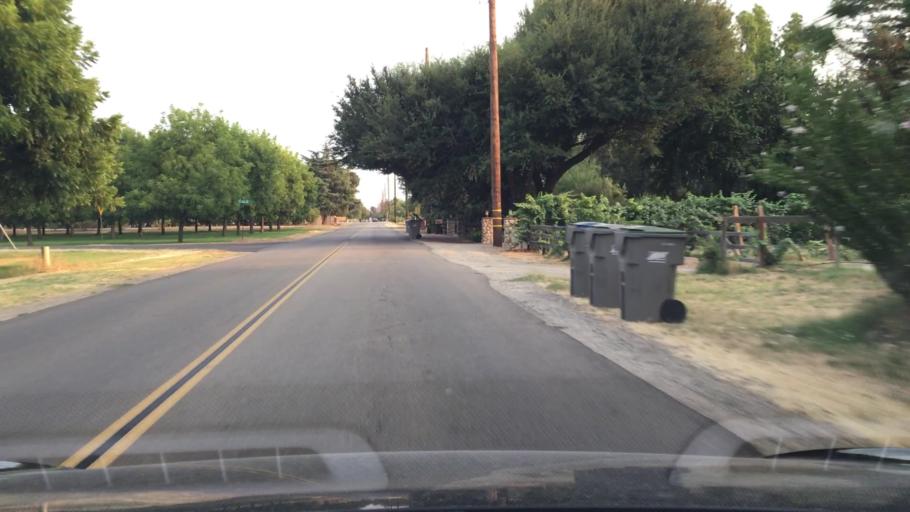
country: US
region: California
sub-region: Fresno County
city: Clovis
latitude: 36.8641
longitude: -119.6931
